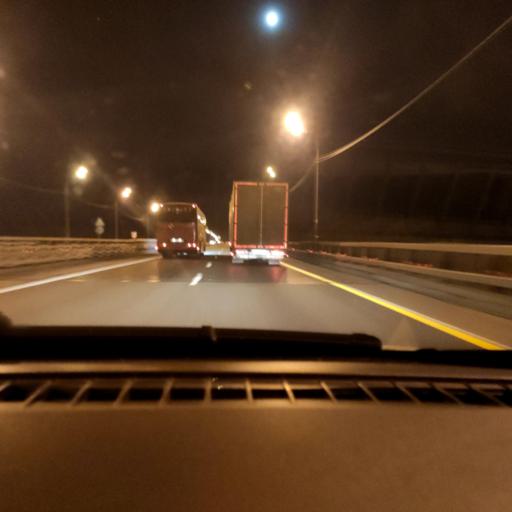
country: RU
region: Lipetsk
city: Khlevnoye
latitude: 52.2365
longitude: 39.0771
